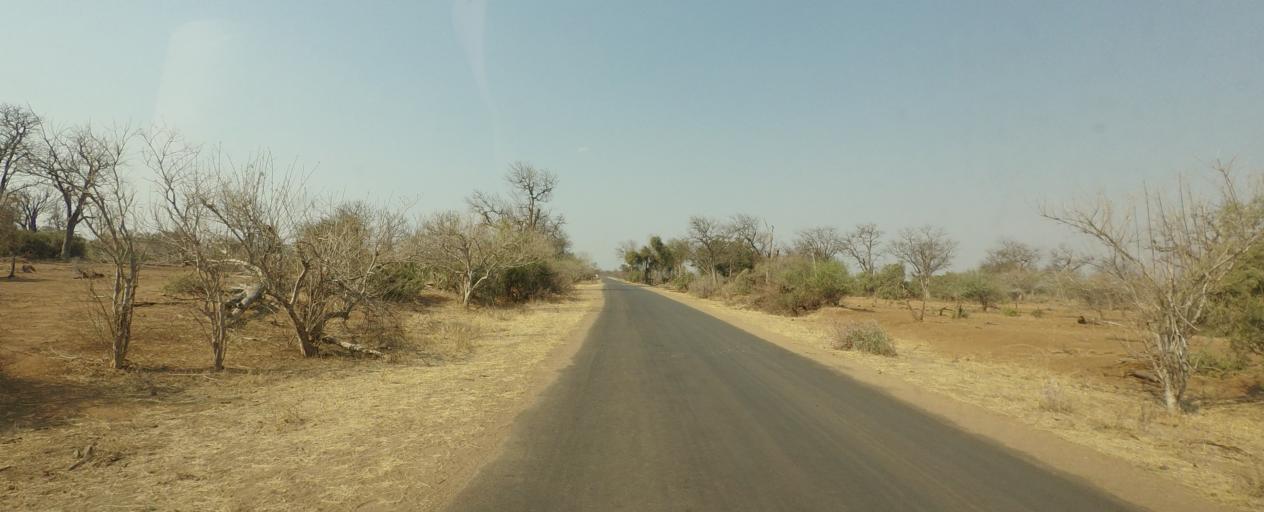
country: ZA
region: Limpopo
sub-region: Mopani District Municipality
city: Giyani
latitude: -23.0953
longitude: 31.4166
